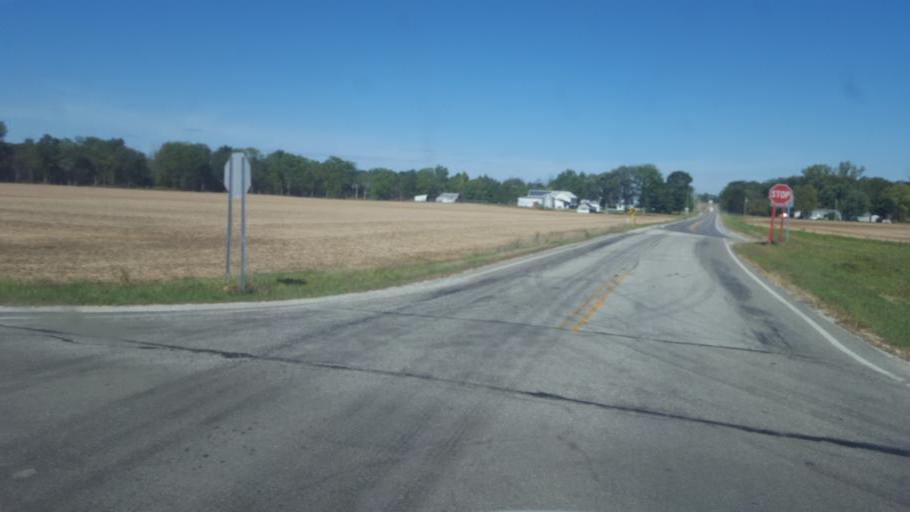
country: US
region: Ohio
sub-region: Crawford County
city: Bucyrus
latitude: 40.8921
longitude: -83.0167
